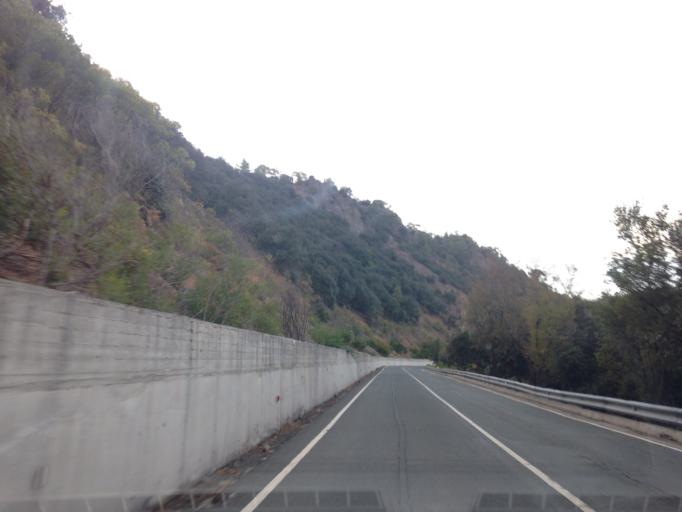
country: CY
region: Lefkosia
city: Kakopetria
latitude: 34.9868
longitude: 32.7423
